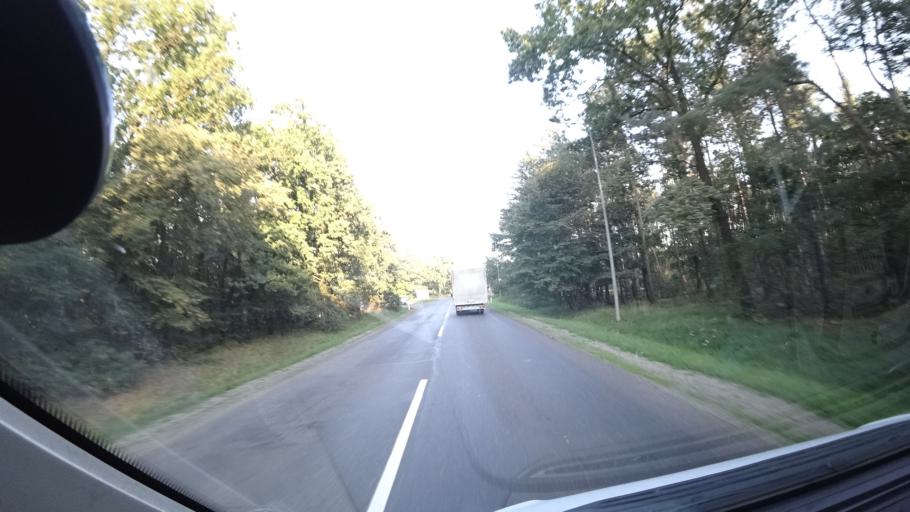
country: PL
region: Opole Voivodeship
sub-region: Powiat kedzierzynsko-kozielski
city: Dziergowice
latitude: 50.2849
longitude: 18.2885
